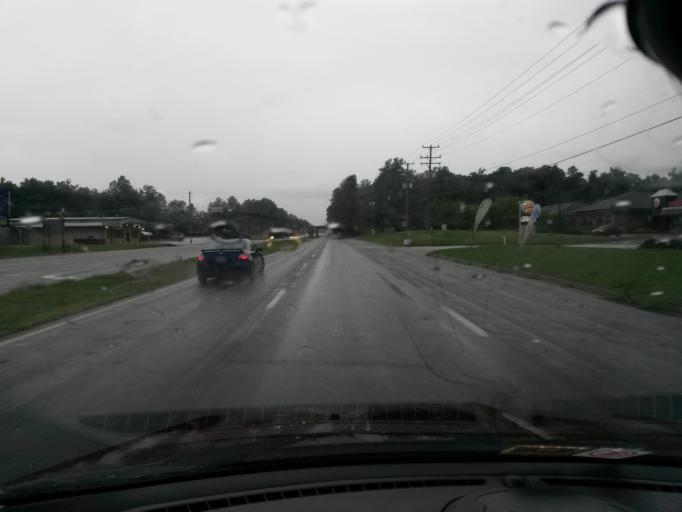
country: US
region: Virginia
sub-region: Chesterfield County
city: Enon
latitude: 37.3347
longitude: -77.3267
